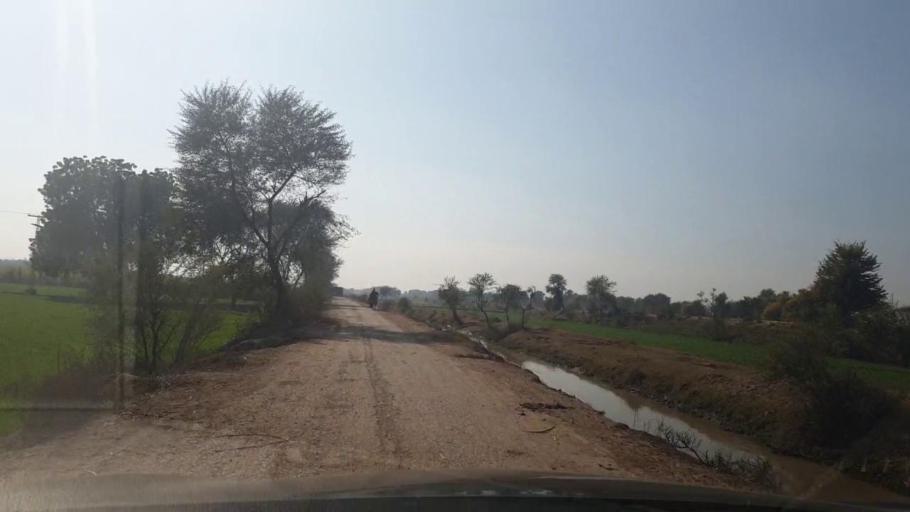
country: PK
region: Sindh
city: Ubauro
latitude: 28.1466
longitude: 69.6896
